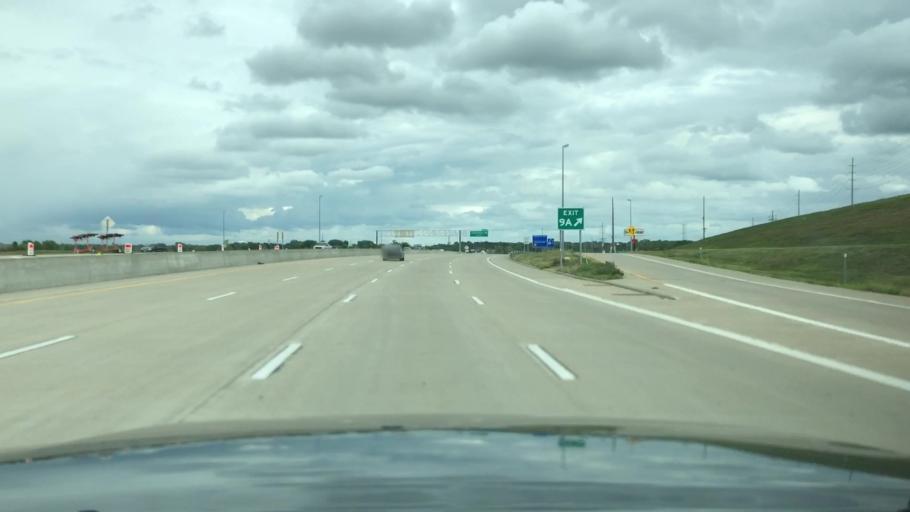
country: US
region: Missouri
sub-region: Saint Charles County
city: Cottleville
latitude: 38.7398
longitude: -90.6225
